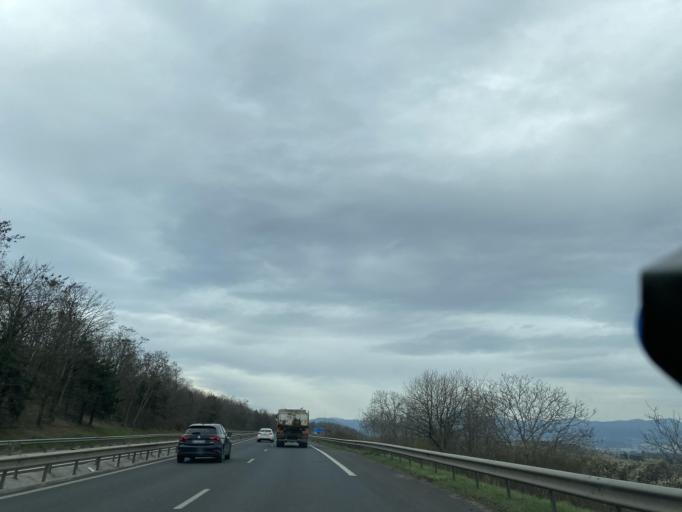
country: FR
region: Auvergne
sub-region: Departement du Puy-de-Dome
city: Aulnat
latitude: 45.7733
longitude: 3.1719
